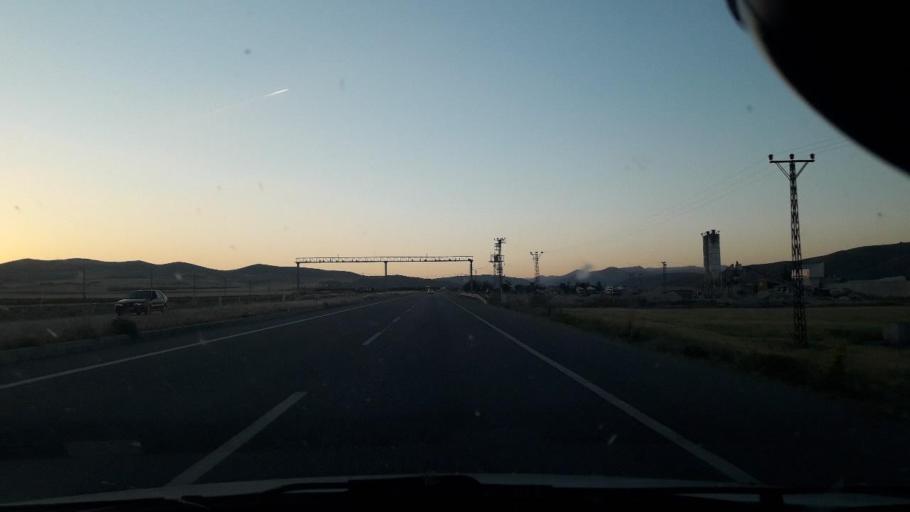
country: TR
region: Malatya
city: Yazihan
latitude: 38.6092
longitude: 38.1757
